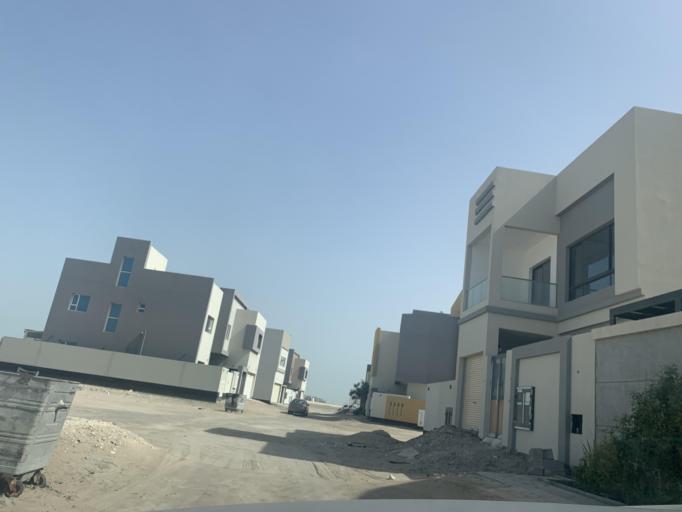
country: BH
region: Northern
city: Sitrah
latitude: 26.1700
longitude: 50.6289
